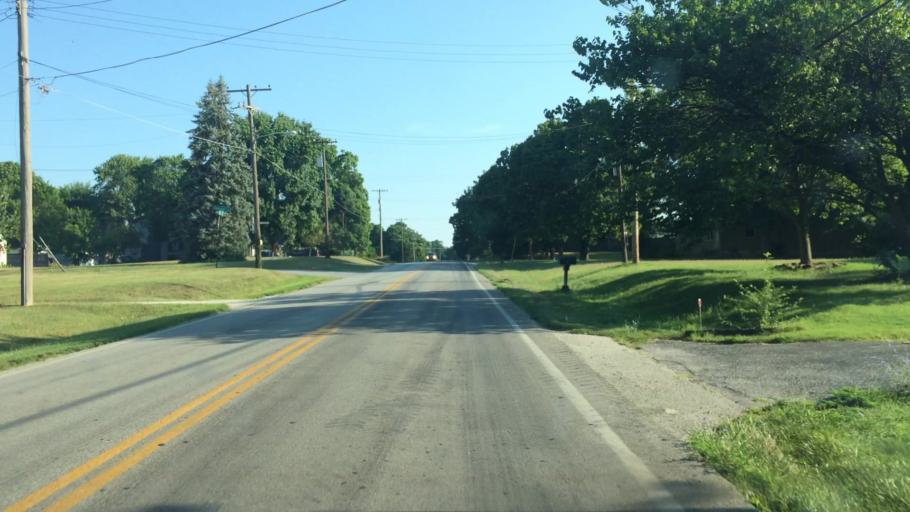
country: US
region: Missouri
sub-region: Greene County
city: Springfield
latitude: 37.2591
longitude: -93.2740
